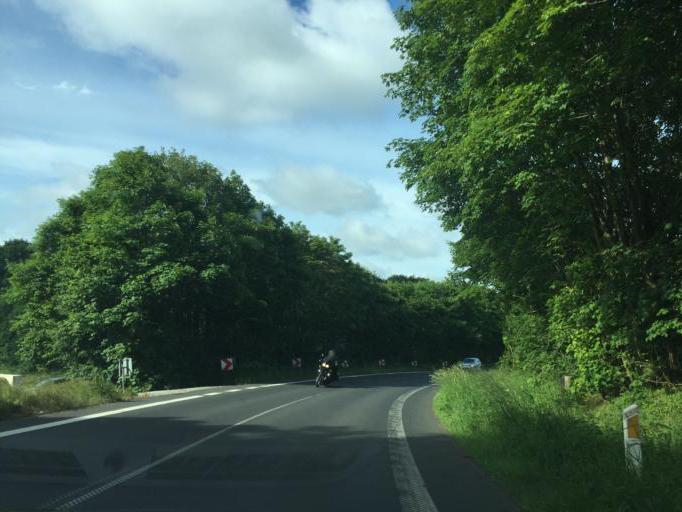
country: DK
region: South Denmark
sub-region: Kolding Kommune
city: Sonder Bjert
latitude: 55.5209
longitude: 9.5435
